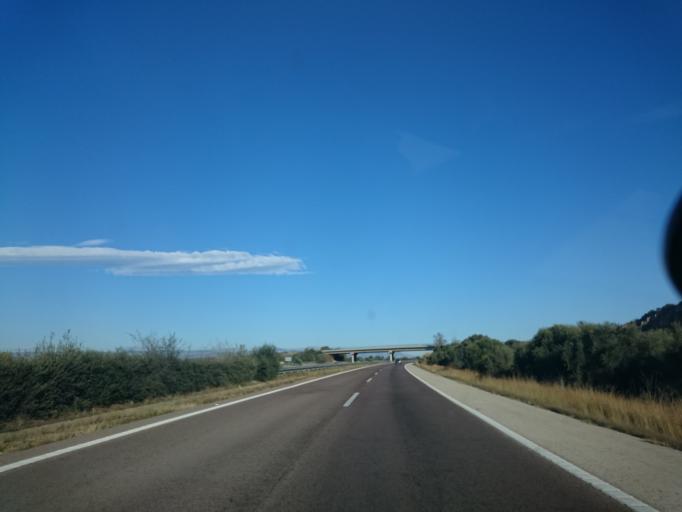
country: ES
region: Valencia
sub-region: Provincia de Castello
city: Vinaros
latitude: 40.4889
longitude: 0.4153
